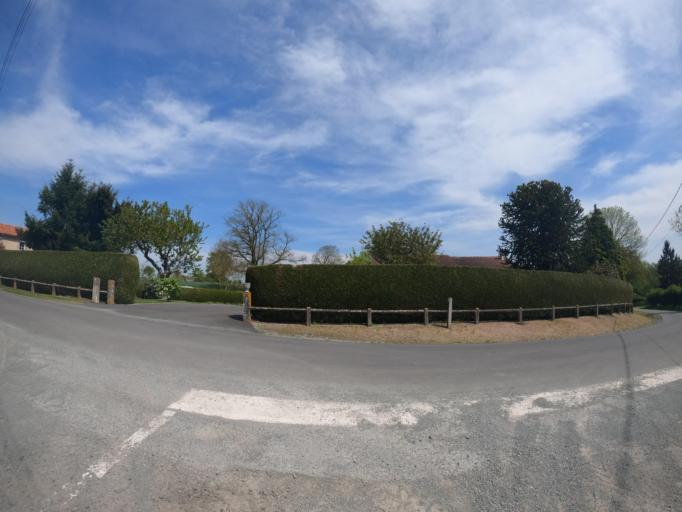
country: FR
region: Poitou-Charentes
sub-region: Departement des Deux-Sevres
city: Moncoutant
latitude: 46.6633
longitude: -0.5268
